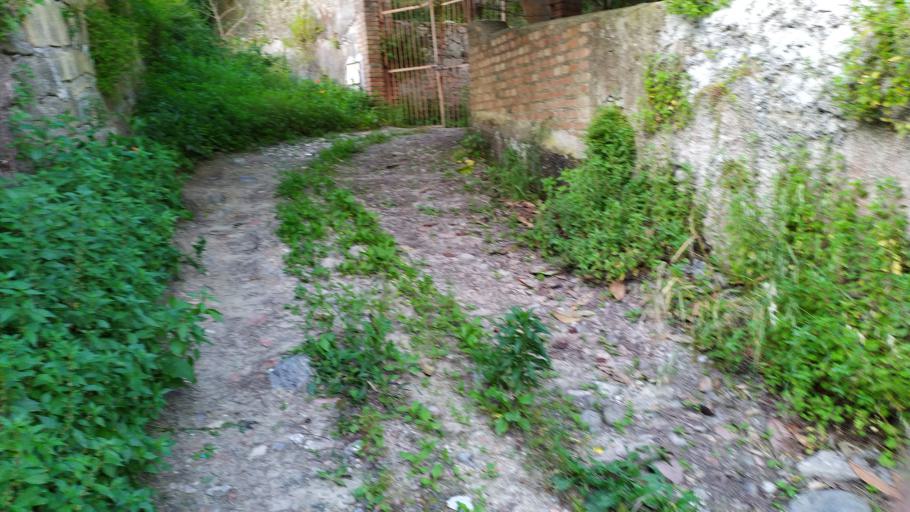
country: IT
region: Sicily
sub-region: Messina
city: Gualtieri Sicamino
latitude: 38.1661
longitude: 15.3237
